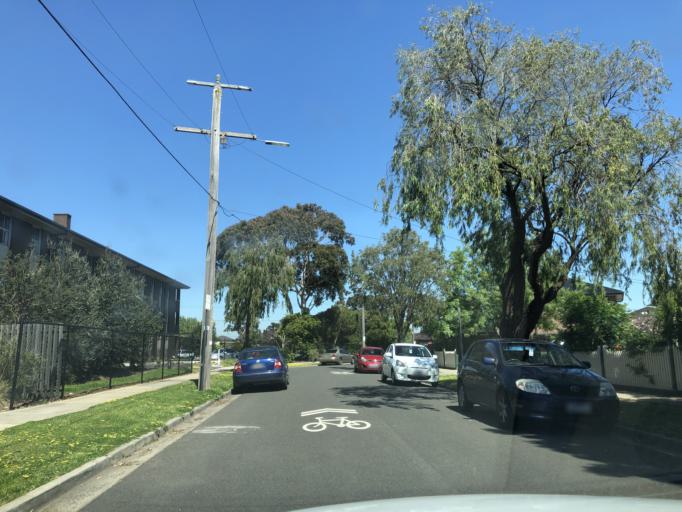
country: AU
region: Victoria
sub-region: Monash
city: Clayton
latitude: -37.9158
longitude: 145.1315
